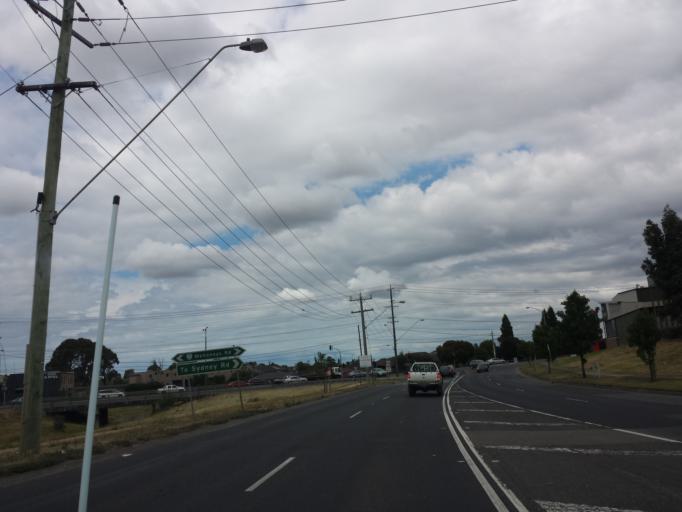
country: AU
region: Victoria
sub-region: Whittlesea
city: Thomastown
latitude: -37.6927
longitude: 145.0017
